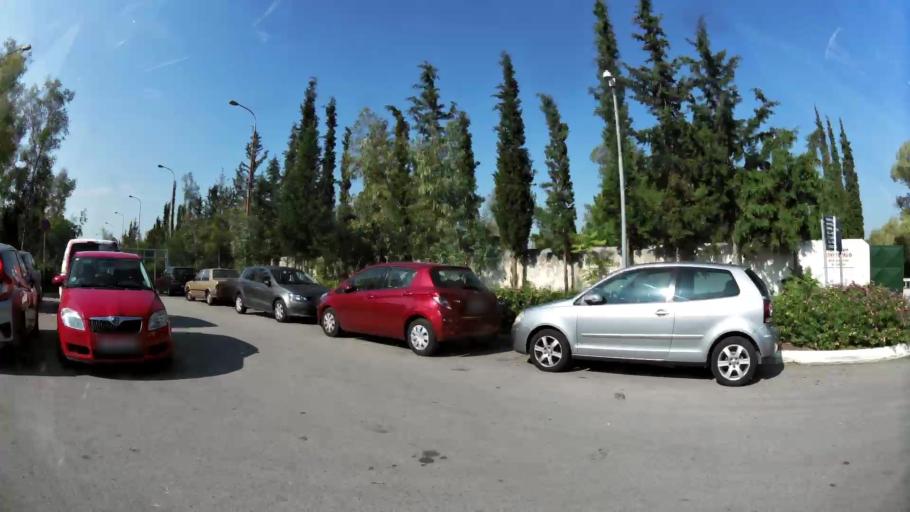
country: GR
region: Attica
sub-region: Nomarchia Athinas
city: Papagou
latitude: 37.9862
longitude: 23.7732
